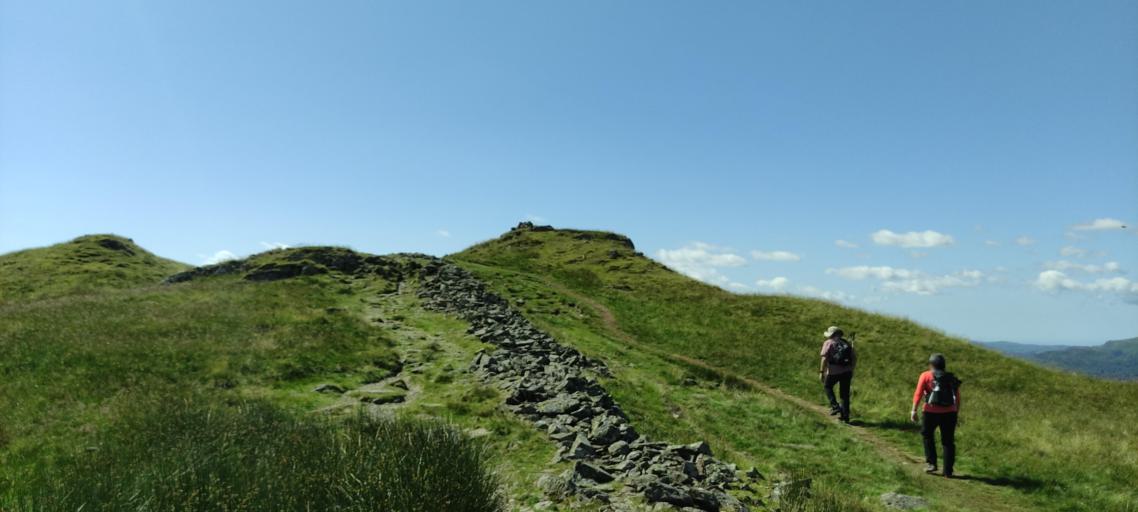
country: GB
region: England
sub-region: Cumbria
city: Ambleside
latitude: 54.4585
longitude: -2.9964
